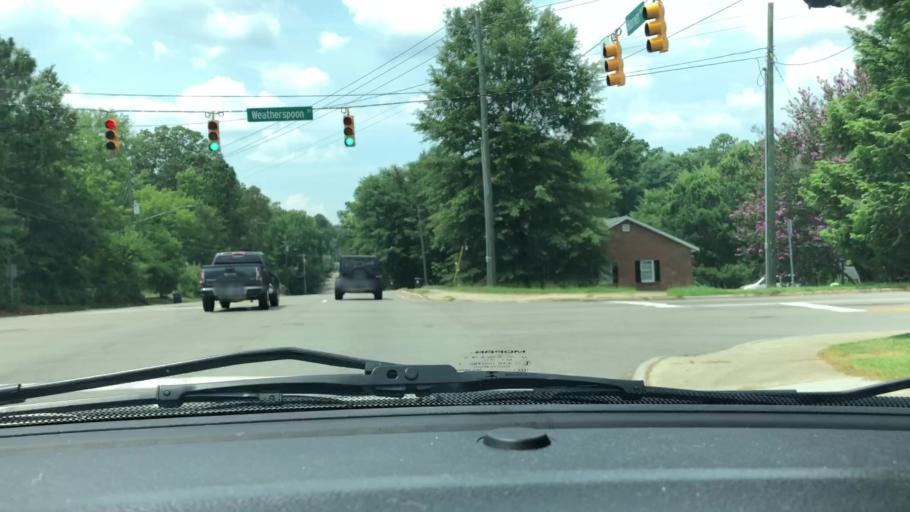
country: US
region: North Carolina
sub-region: Lee County
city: Sanford
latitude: 35.4855
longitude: -79.1852
